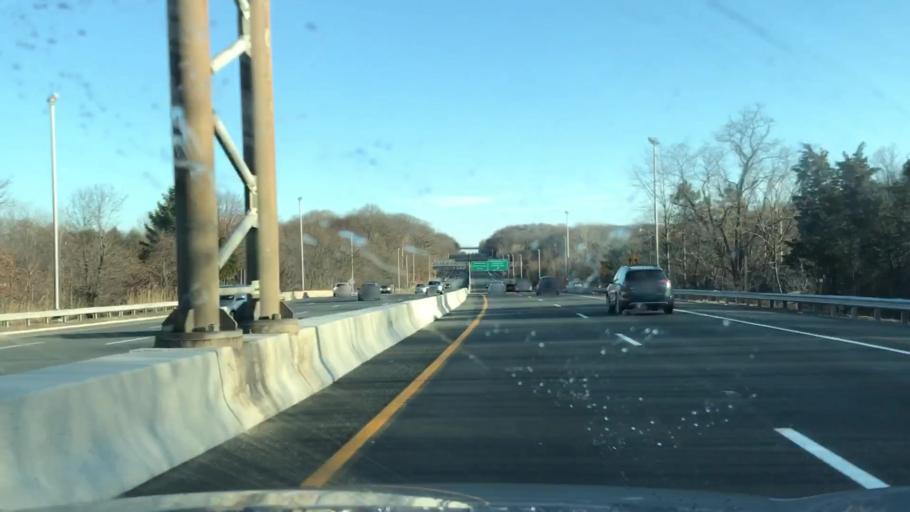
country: US
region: New Jersey
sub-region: Bergen County
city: Franklin Lakes
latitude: 41.0187
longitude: -74.2199
